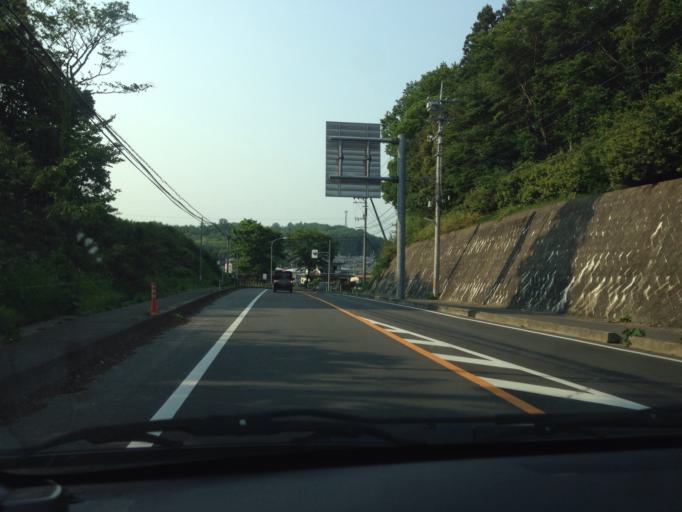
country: JP
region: Tochigi
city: Kuroiso
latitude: 37.1002
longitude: 140.1970
